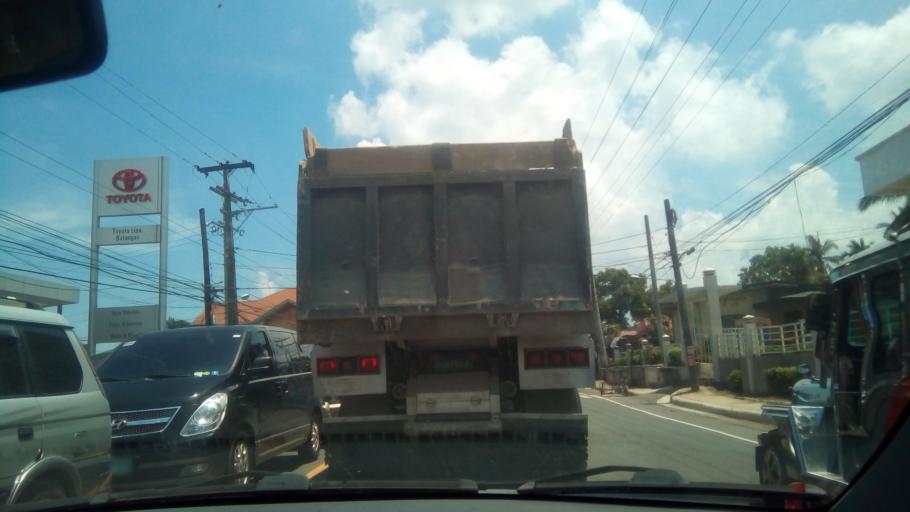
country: PH
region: Calabarzon
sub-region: Province of Batangas
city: Banaybanay
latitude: 13.9418
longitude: 121.1361
